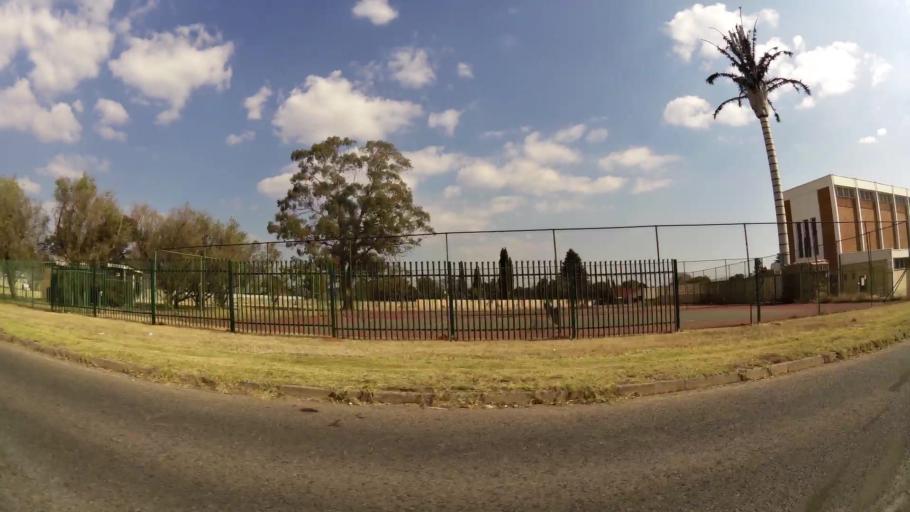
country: ZA
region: Gauteng
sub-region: City of Johannesburg Metropolitan Municipality
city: Modderfontein
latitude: -26.0941
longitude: 28.2507
